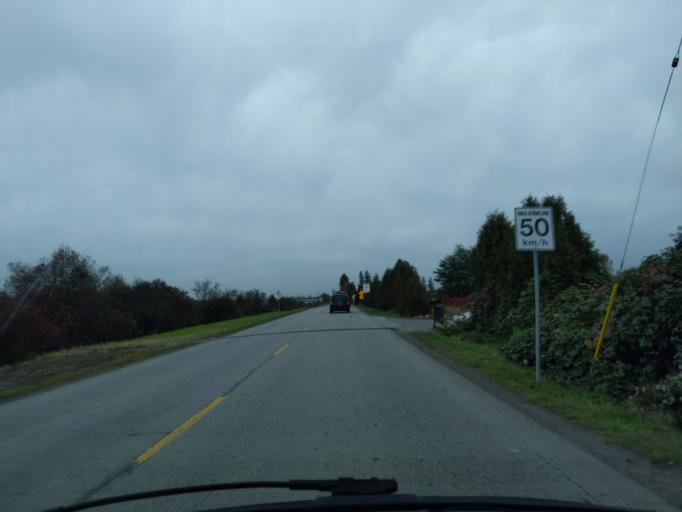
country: CA
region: British Columbia
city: Pitt Meadows
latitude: 49.2225
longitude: -122.7018
